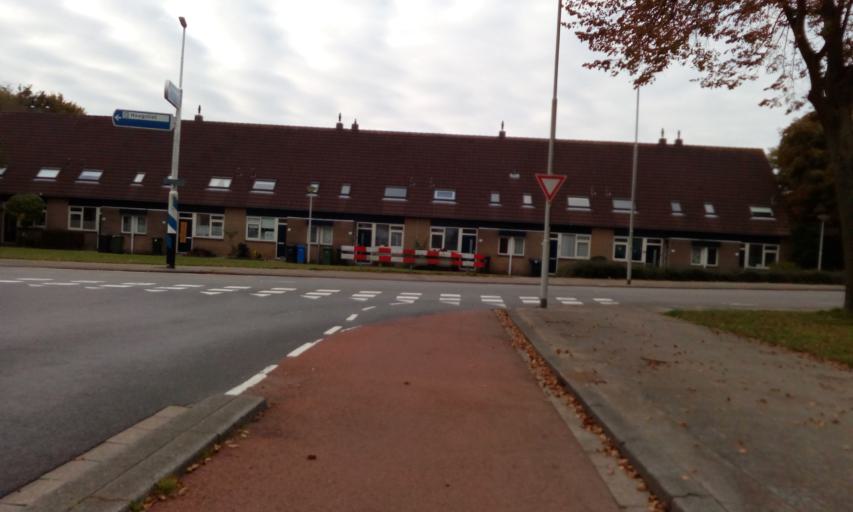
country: NL
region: South Holland
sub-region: Gemeente Spijkenisse
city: Spijkenisse
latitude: 51.8597
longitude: 4.3646
